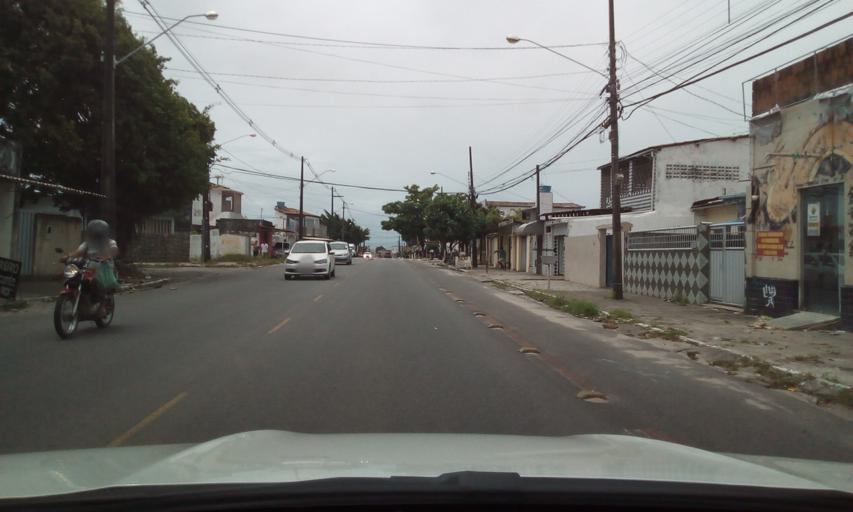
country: BR
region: Paraiba
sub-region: Joao Pessoa
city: Joao Pessoa
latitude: -7.1813
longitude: -34.8387
